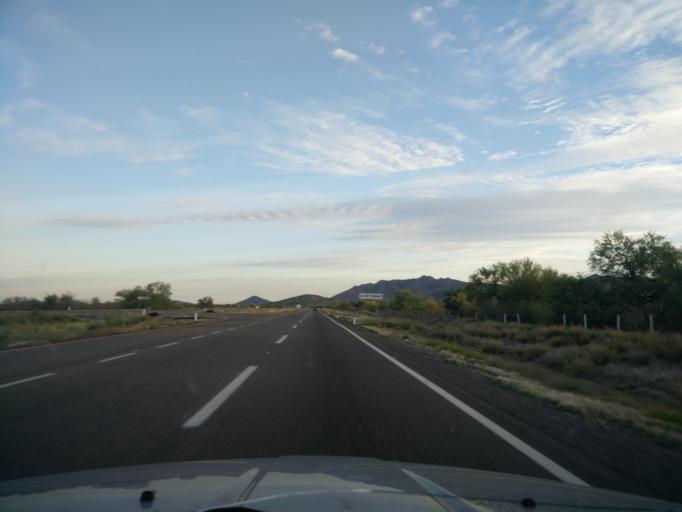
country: MX
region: Sonora
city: Hermosillo
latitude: 28.9237
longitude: -110.9526
